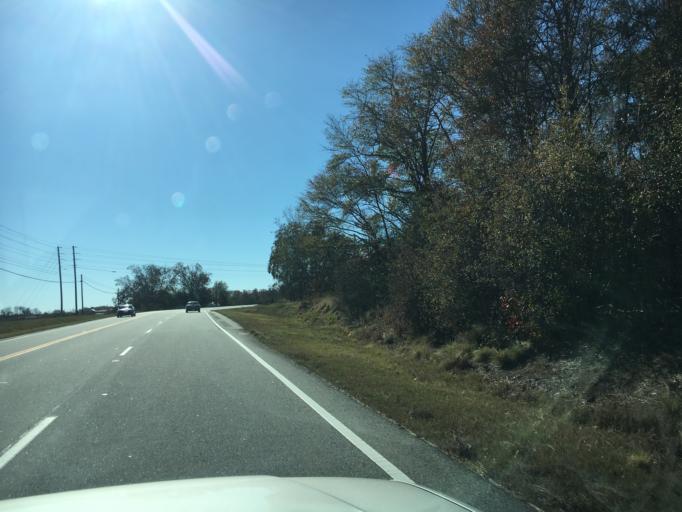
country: US
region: Georgia
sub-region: Hart County
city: Hartwell
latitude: 34.3223
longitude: -82.9787
